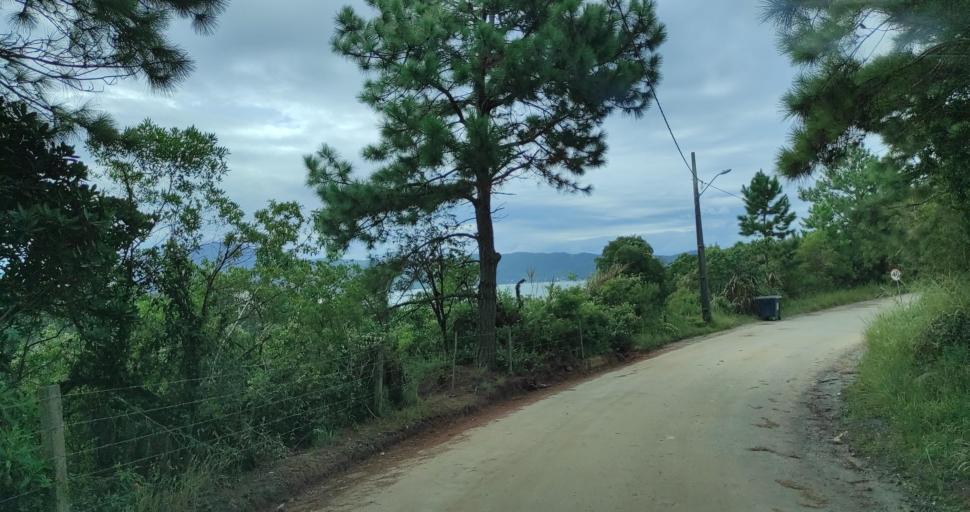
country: BR
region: Santa Catarina
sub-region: Porto Belo
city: Porto Belo
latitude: -27.2163
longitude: -48.5073
